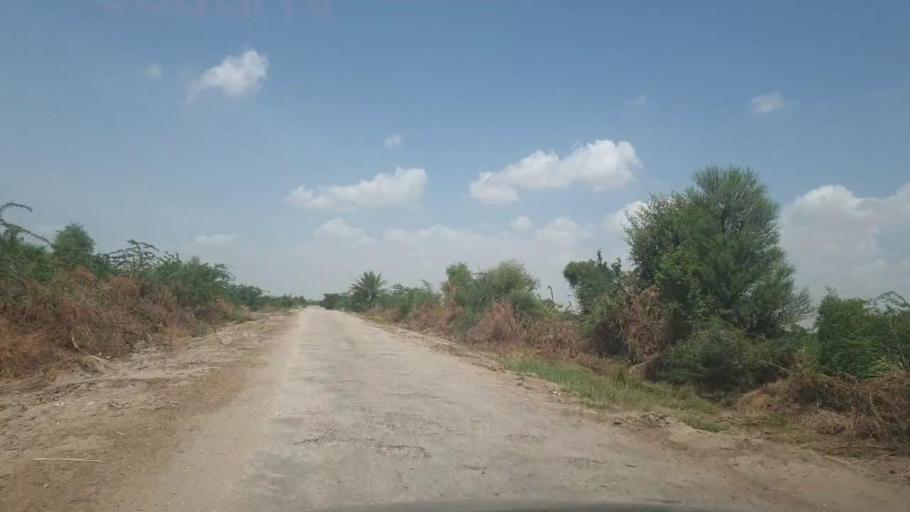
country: PK
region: Sindh
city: Kot Diji
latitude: 27.2170
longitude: 69.0363
